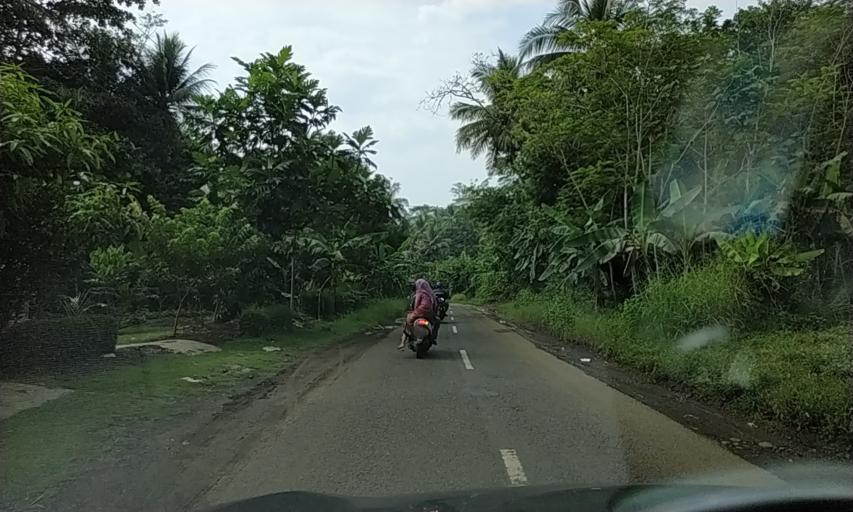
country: ID
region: Central Java
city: Meluwung
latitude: -7.3806
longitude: 108.7005
